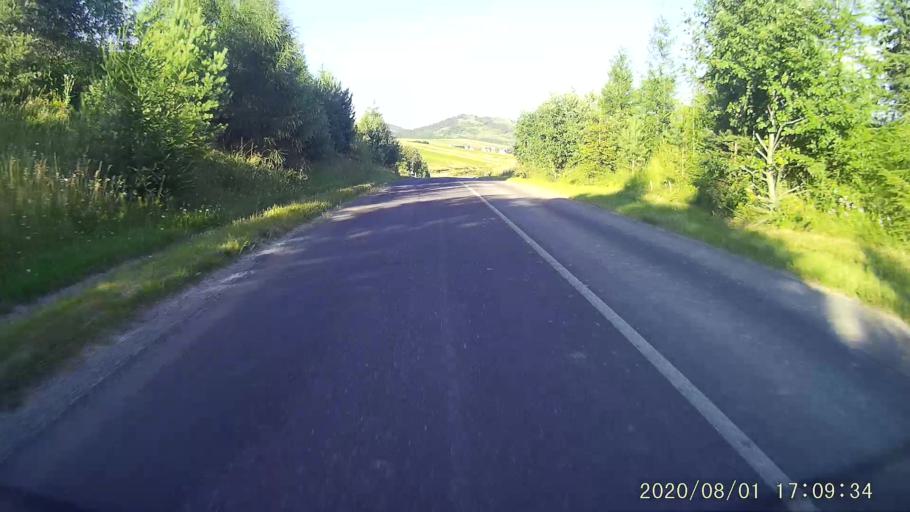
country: SK
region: Presovsky
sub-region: Okres Poprad
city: Zdiar
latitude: 49.2333
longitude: 20.3365
